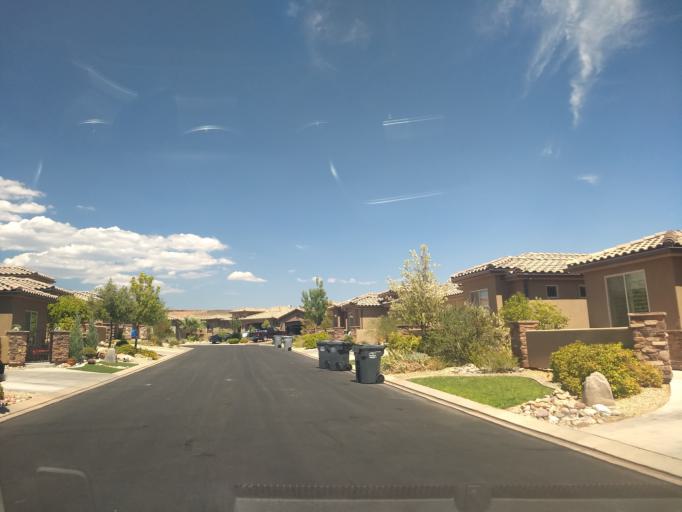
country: US
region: Utah
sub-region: Washington County
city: Washington
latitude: 37.1402
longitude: -113.4821
